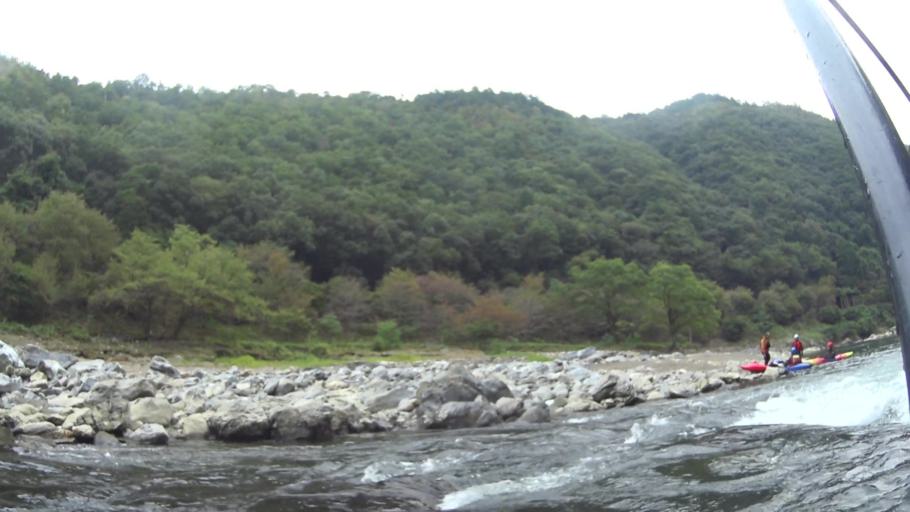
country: JP
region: Kyoto
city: Kameoka
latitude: 35.0259
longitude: 135.6535
